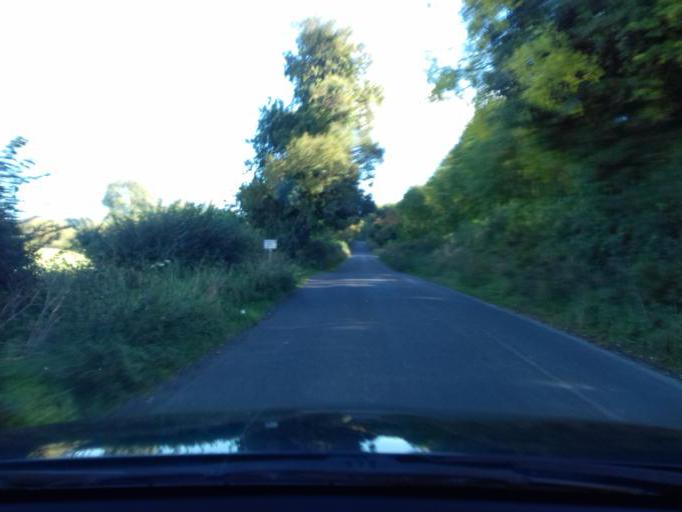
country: IE
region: Leinster
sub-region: An Mhi
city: Duleek
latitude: 53.6851
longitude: -6.4758
